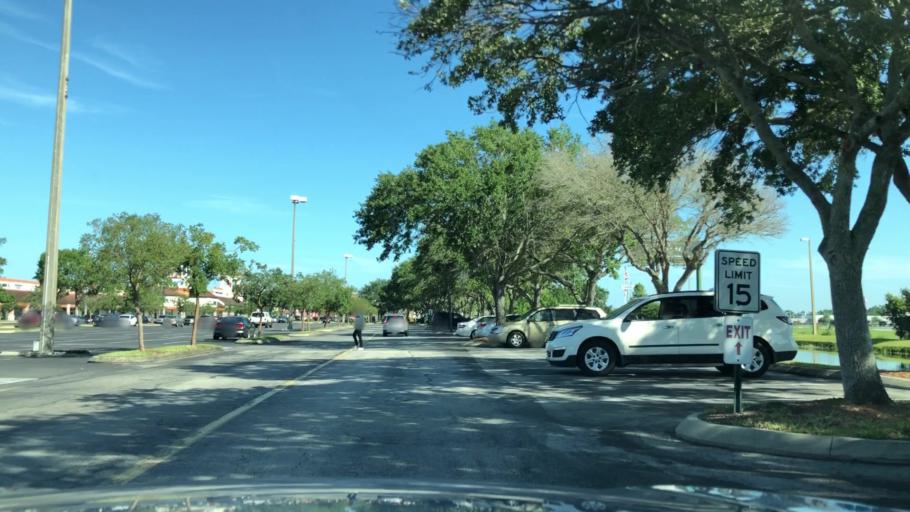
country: US
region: Florida
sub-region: Saint Johns County
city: Saint Augustine
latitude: 29.9223
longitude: -81.4147
